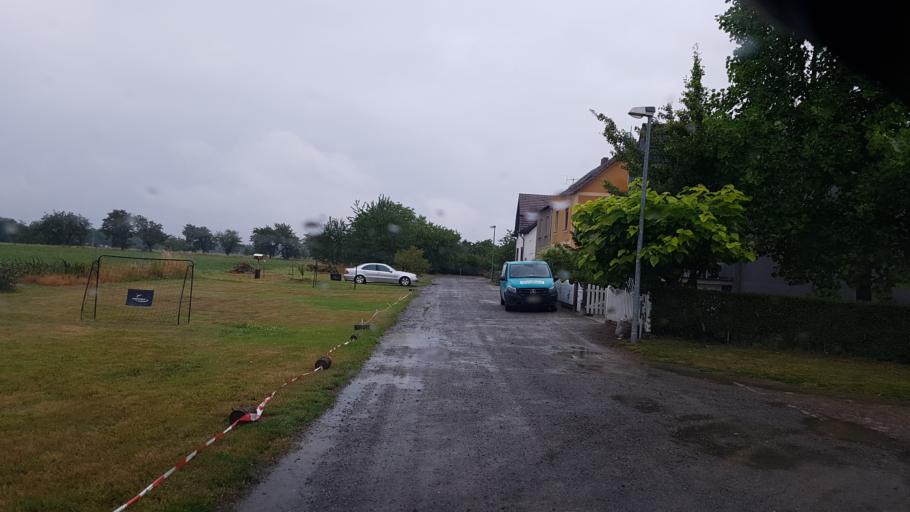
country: DE
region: Brandenburg
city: Dahme
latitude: 51.8660
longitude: 13.4148
